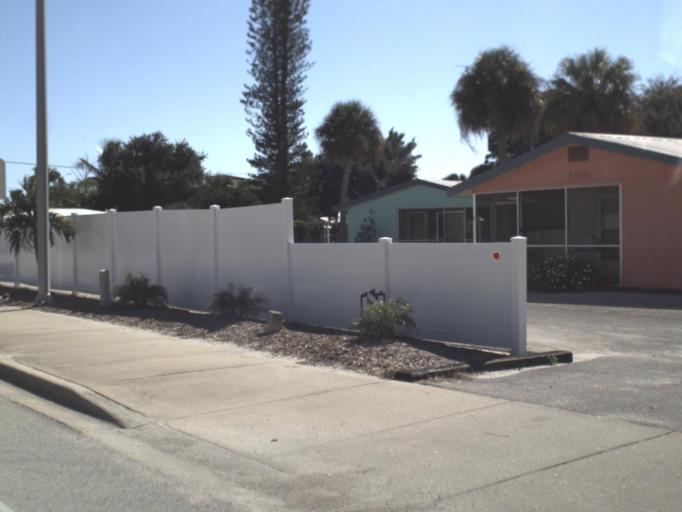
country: US
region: Florida
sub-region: Charlotte County
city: Manasota Key
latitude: 26.9436
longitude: -82.3504
